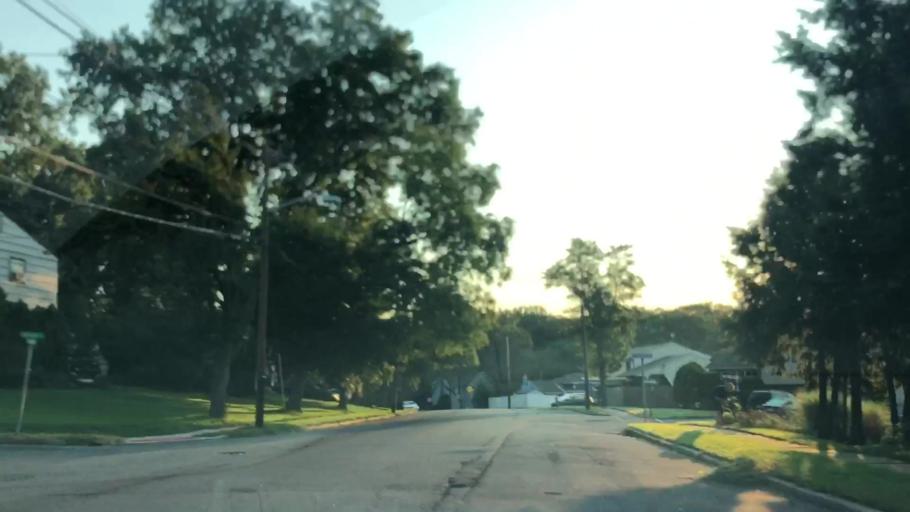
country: US
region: New Jersey
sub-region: Union County
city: Winfield
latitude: 40.6263
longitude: -74.2887
